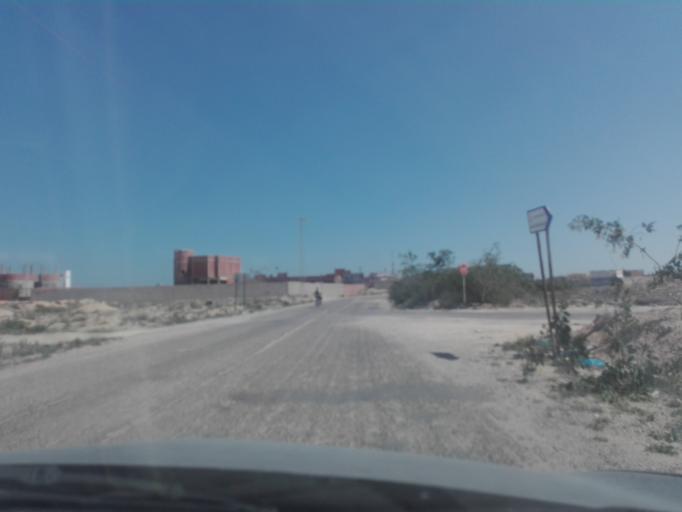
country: TN
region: Qabis
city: Gabes
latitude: 33.8706
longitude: 10.0450
